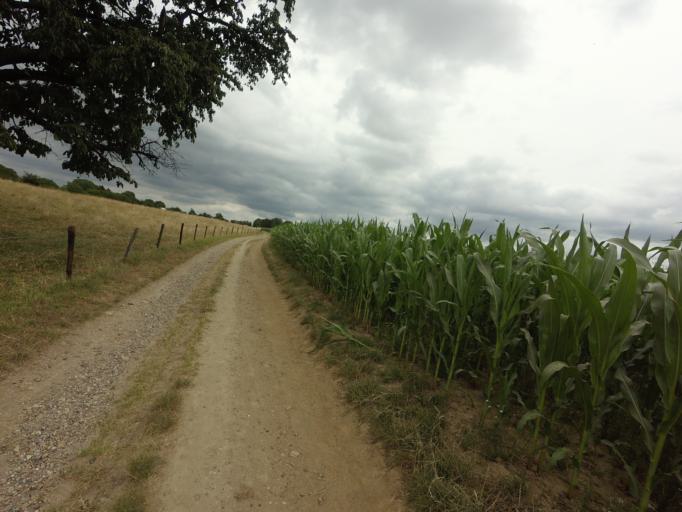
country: NL
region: Limburg
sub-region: Valkenburg aan de Geul
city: Sibbe
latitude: 50.8365
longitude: 5.8255
